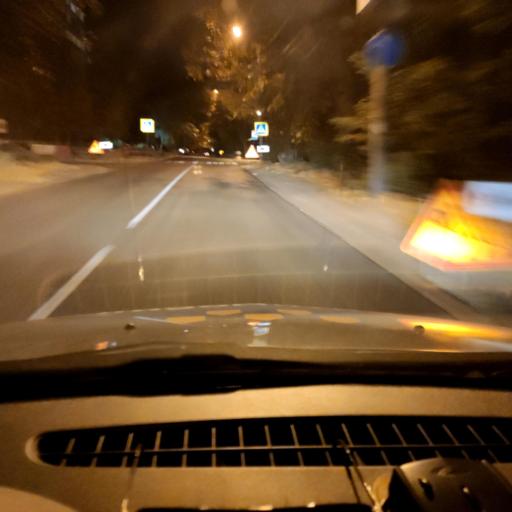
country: RU
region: Voronezj
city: Voronezh
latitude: 51.7199
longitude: 39.2239
